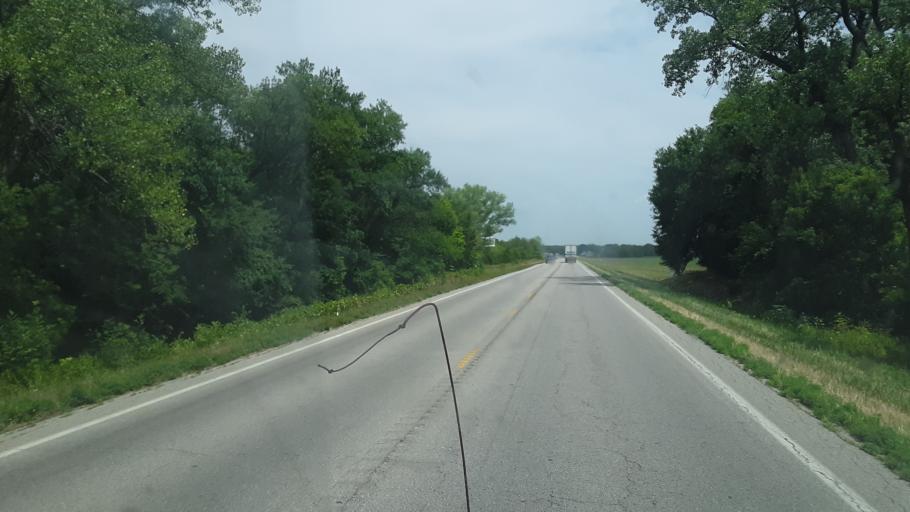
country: US
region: Kansas
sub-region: Bourbon County
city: Fort Scott
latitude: 37.8577
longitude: -94.7235
